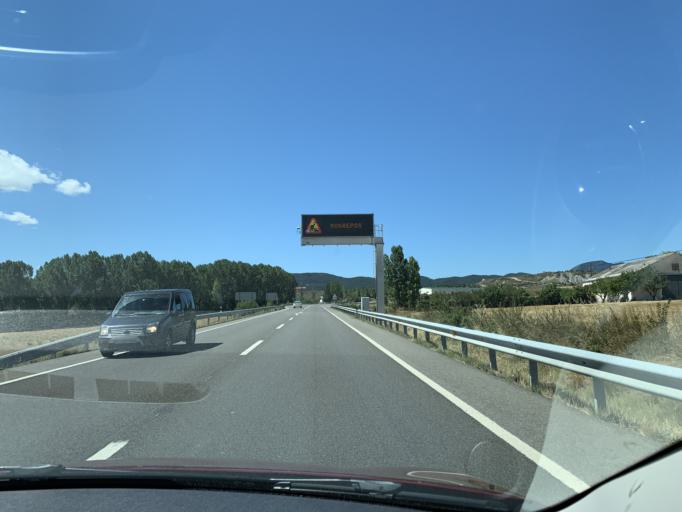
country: ES
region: Aragon
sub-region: Provincia de Huesca
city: Sabinanigo
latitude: 42.5384
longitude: -0.3582
